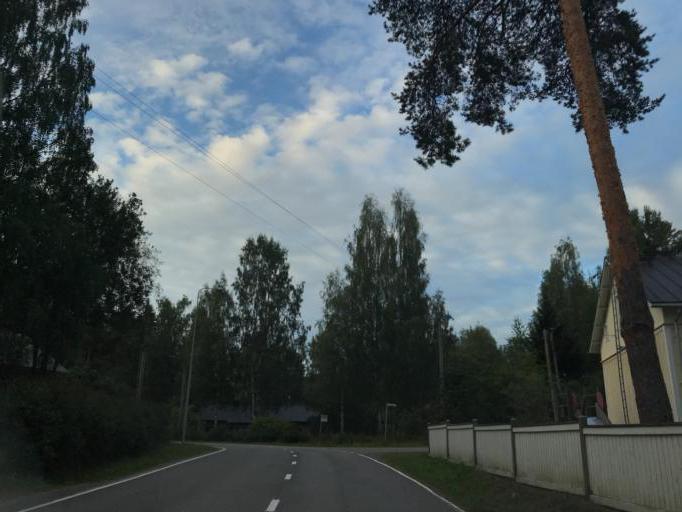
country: FI
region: Uusimaa
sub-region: Helsinki
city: Vihti
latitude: 60.4016
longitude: 24.4930
